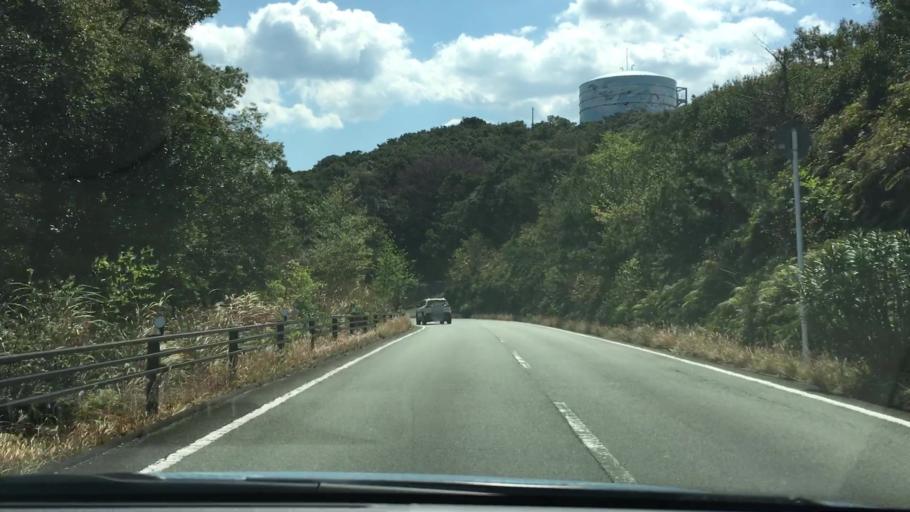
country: JP
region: Mie
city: Toba
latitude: 34.4493
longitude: 136.9067
